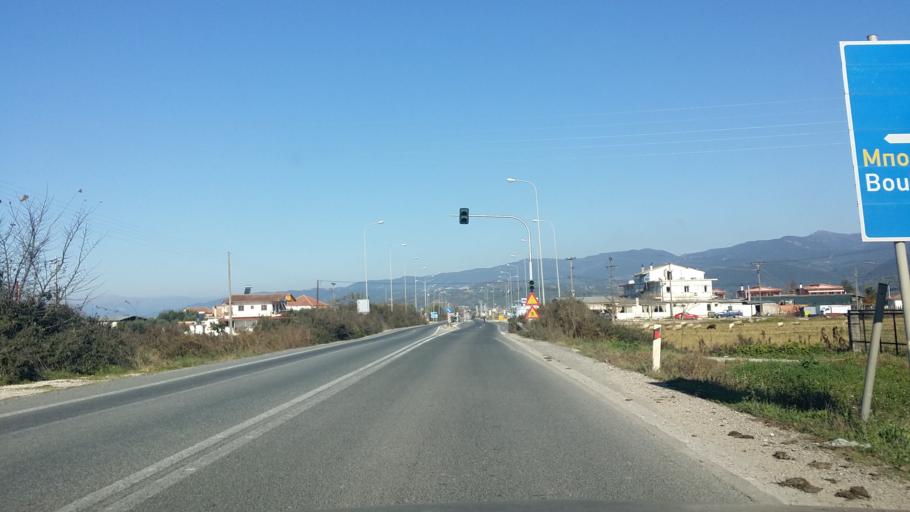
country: GR
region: West Greece
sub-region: Nomos Aitolias kai Akarnanias
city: Krikellos
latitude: 38.9282
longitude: 21.1774
